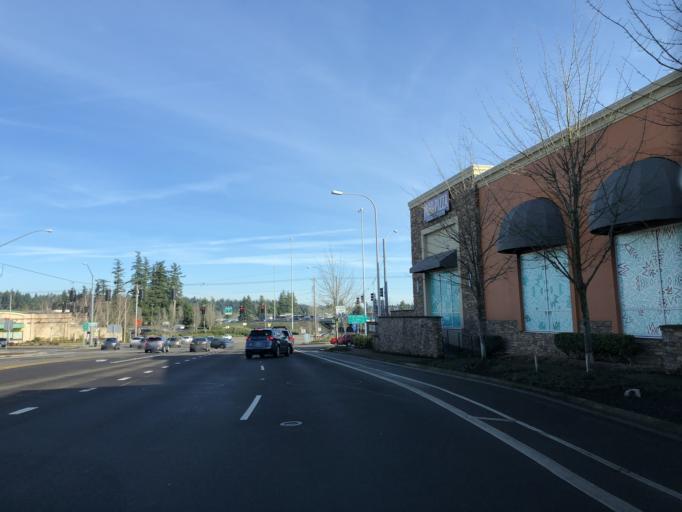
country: US
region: Oregon
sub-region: Washington County
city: Durham
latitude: 45.3954
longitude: -122.7507
